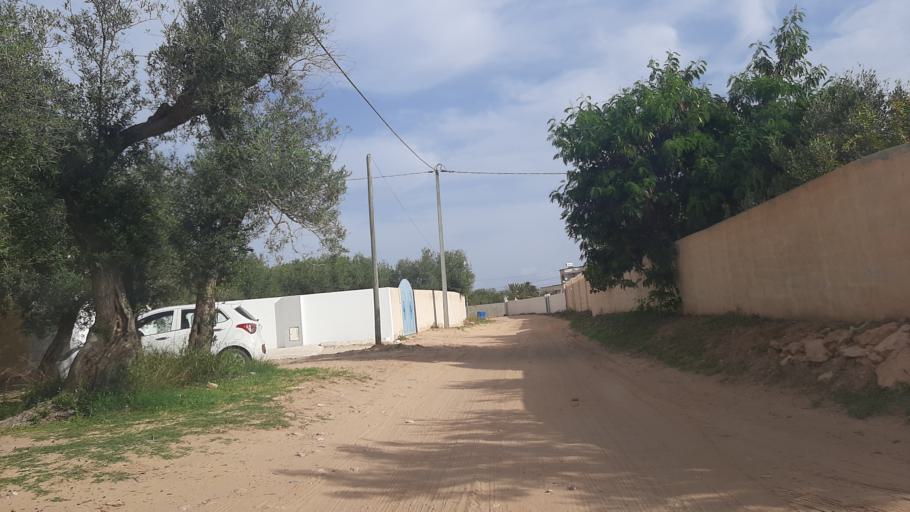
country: TN
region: Madanin
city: Midoun
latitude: 33.8104
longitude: 11.0252
